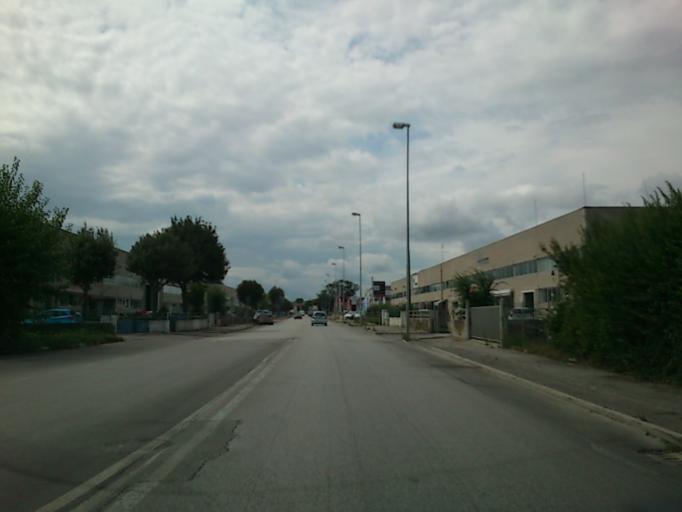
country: IT
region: The Marches
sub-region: Provincia di Pesaro e Urbino
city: Fano
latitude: 43.8309
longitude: 13.0425
